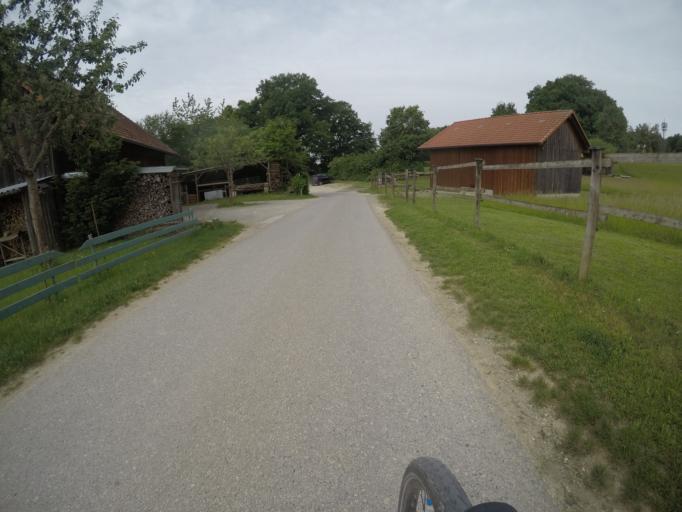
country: DE
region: Baden-Wuerttemberg
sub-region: Tuebingen Region
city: Pliezhausen
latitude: 48.5955
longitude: 9.1687
